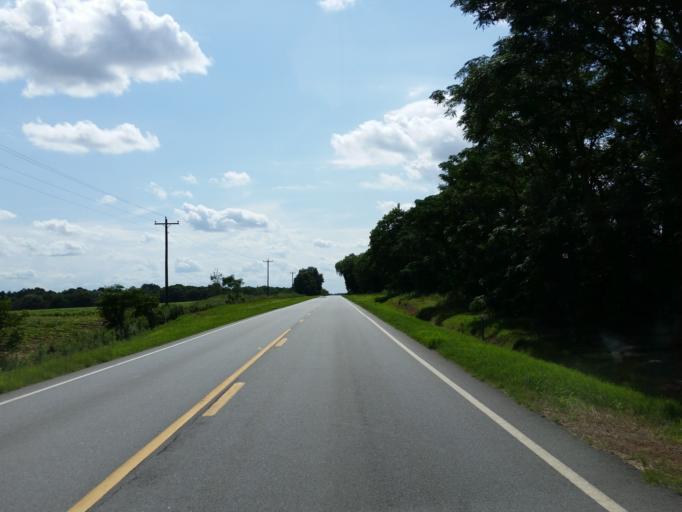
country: US
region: Georgia
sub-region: Turner County
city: Ashburn
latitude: 31.6358
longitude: -83.4816
